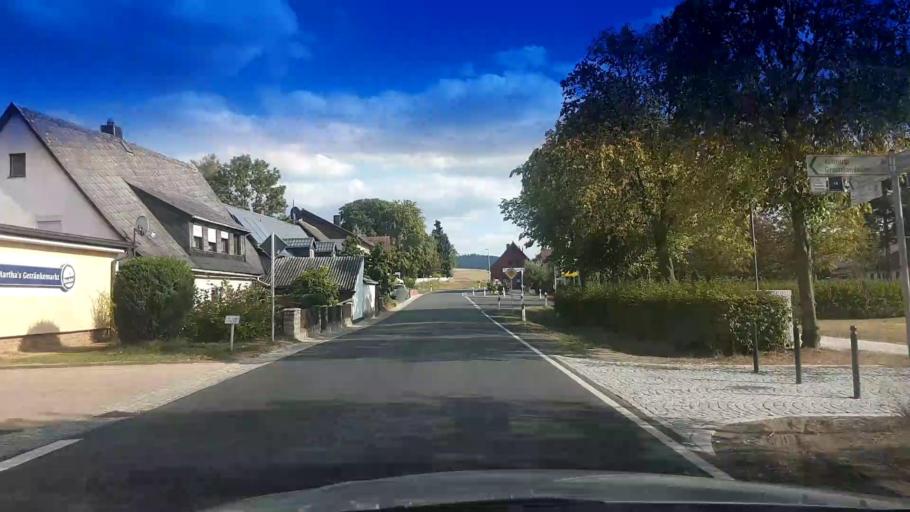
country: DE
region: Bavaria
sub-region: Upper Palatinate
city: Neualbenreuth
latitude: 49.9788
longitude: 12.4439
